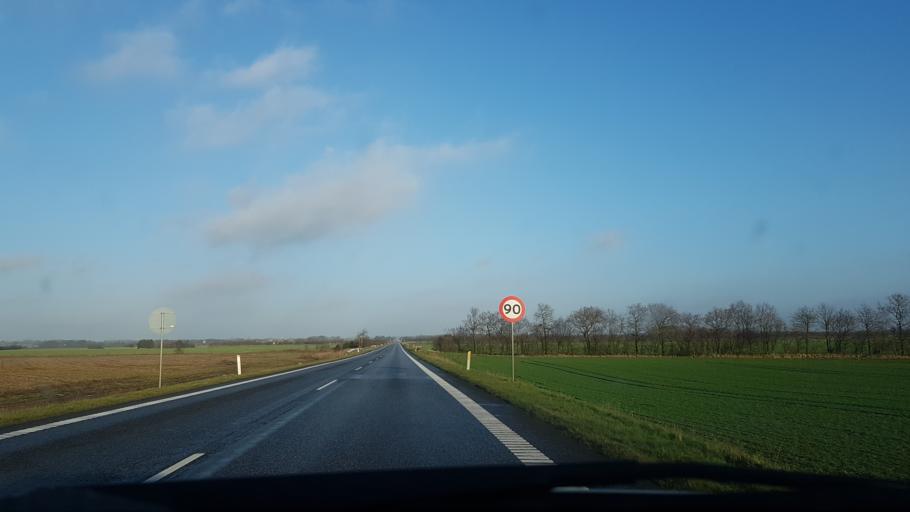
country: DK
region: South Denmark
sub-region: Tonder Kommune
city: Toftlund
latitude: 55.2163
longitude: 9.1025
